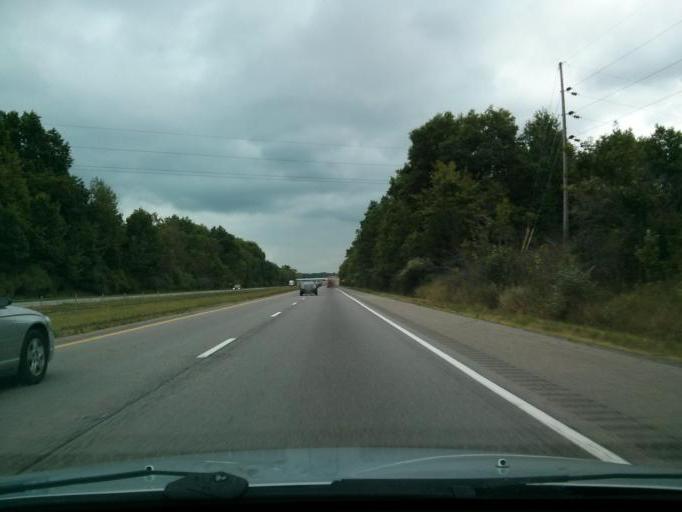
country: US
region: Ohio
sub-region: Mahoning County
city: Craig Beach
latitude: 41.0999
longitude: -80.9971
